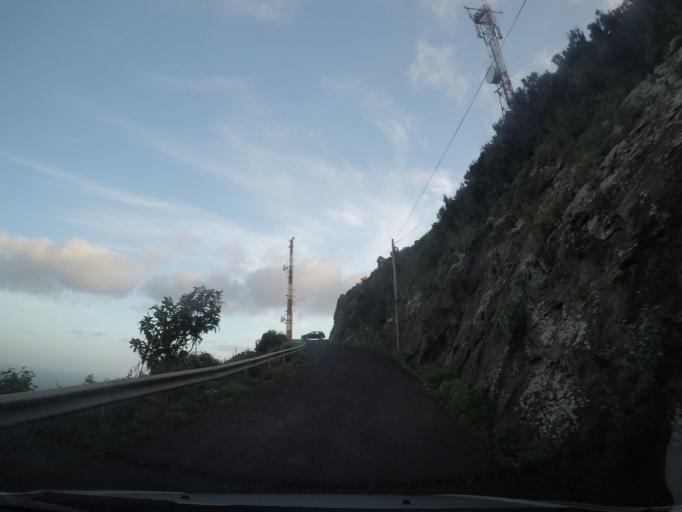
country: PT
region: Madeira
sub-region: Machico
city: Canical
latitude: 32.7244
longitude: -16.7589
